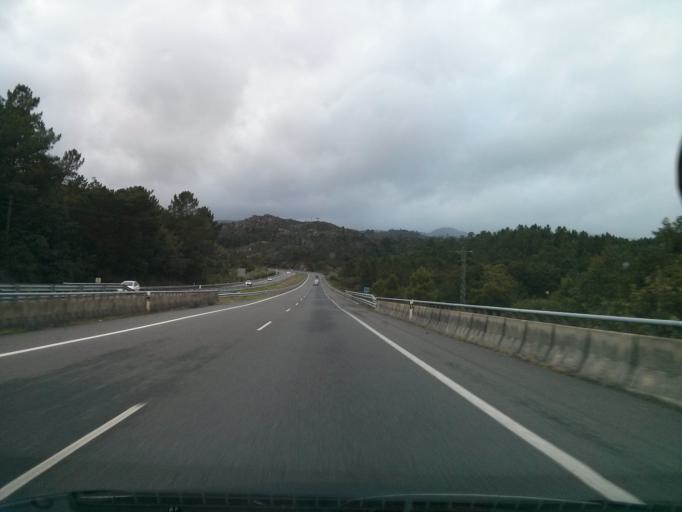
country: ES
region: Galicia
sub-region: Provincia de Ourense
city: Carballeda de Avia
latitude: 42.3095
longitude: -8.1636
